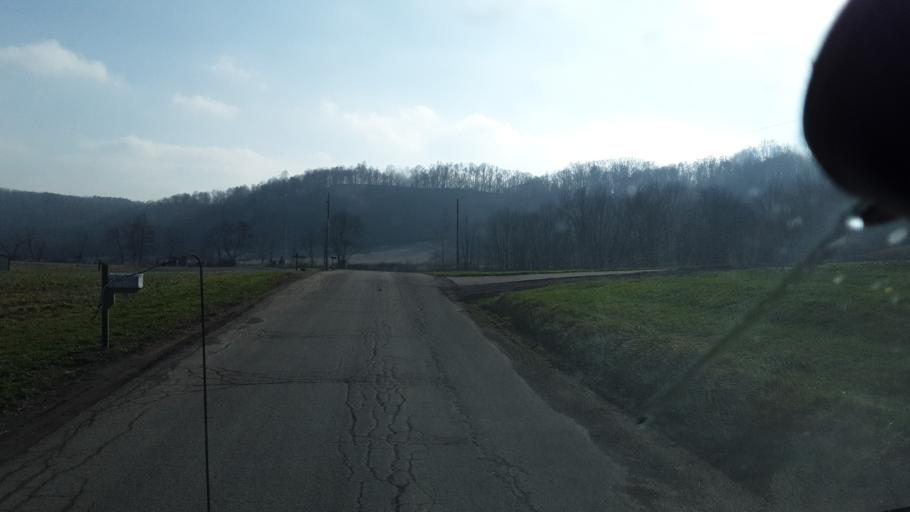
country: US
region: Ohio
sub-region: Knox County
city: Oak Hill
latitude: 40.4316
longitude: -82.2032
